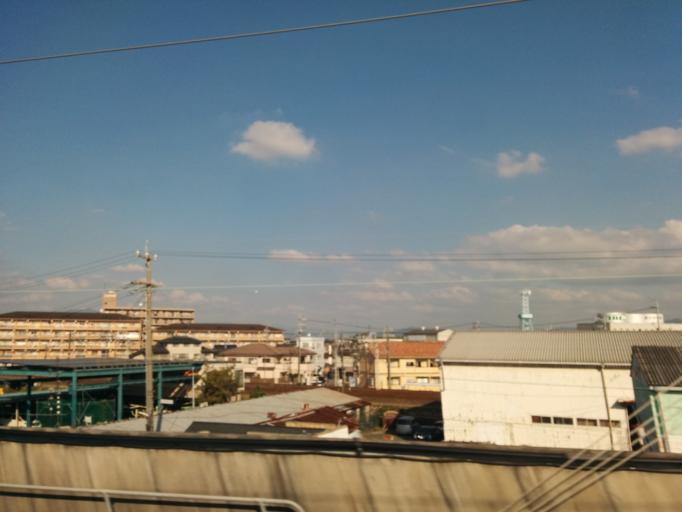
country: JP
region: Aichi
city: Toyohashi
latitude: 34.7735
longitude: 137.3746
